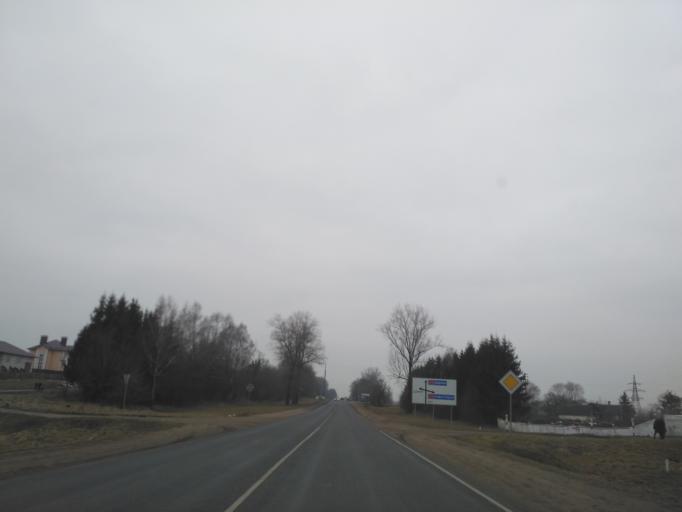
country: BY
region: Brest
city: Baranovichi
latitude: 53.1681
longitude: 26.0308
